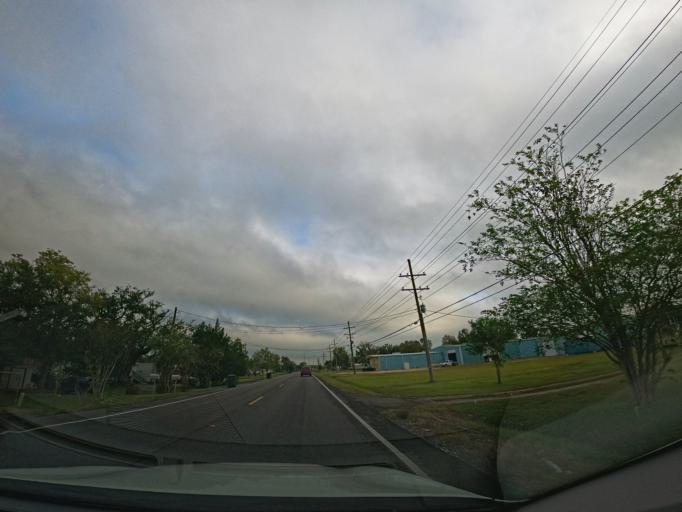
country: US
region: Louisiana
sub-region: Terrebonne Parish
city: Presquille
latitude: 29.5145
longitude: -90.6756
